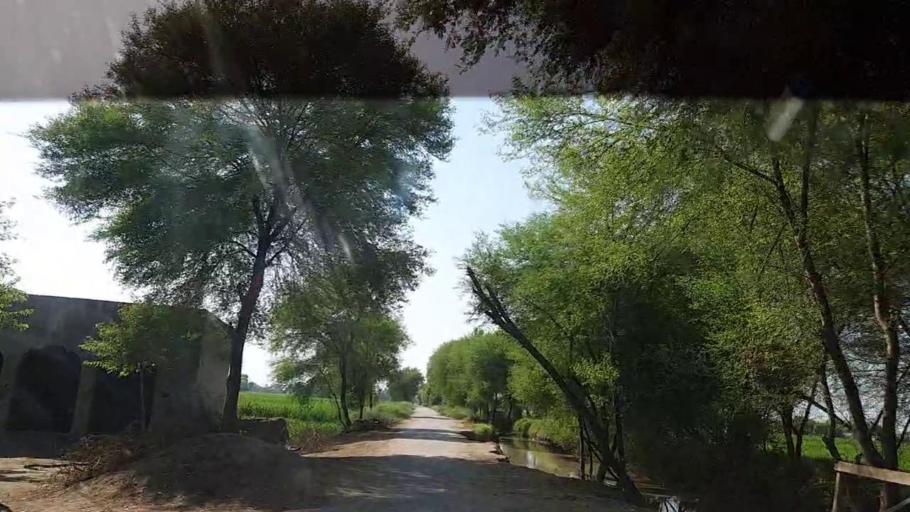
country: PK
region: Sindh
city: Ghauspur
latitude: 28.1736
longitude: 69.0539
